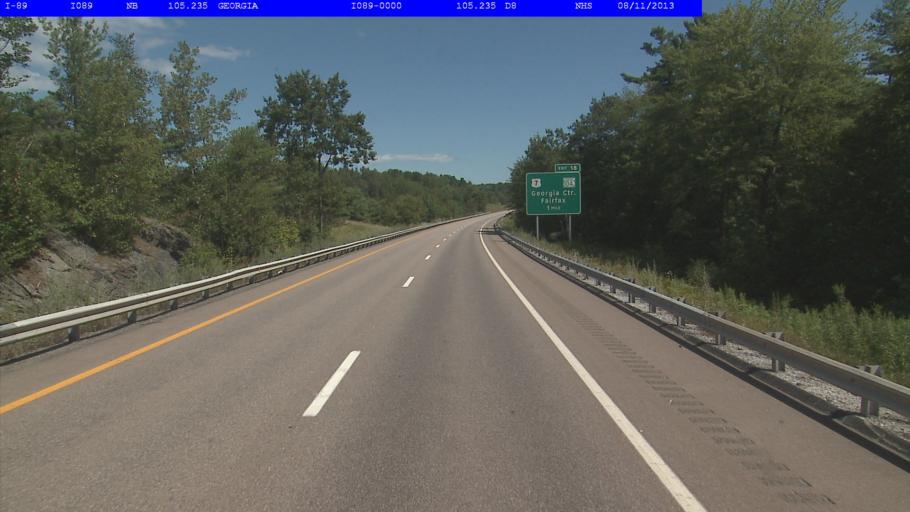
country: US
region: Vermont
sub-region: Chittenden County
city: Milton
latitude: 44.6877
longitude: -73.1266
